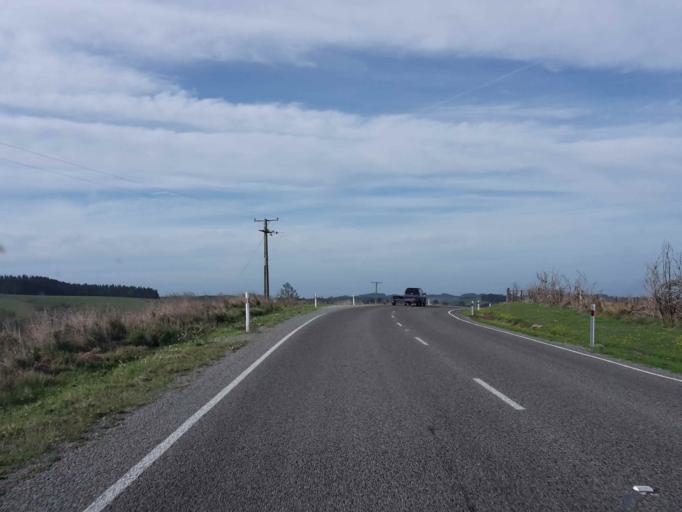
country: NZ
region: Canterbury
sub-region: Timaru District
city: Pleasant Point
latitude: -44.1217
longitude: 171.1114
